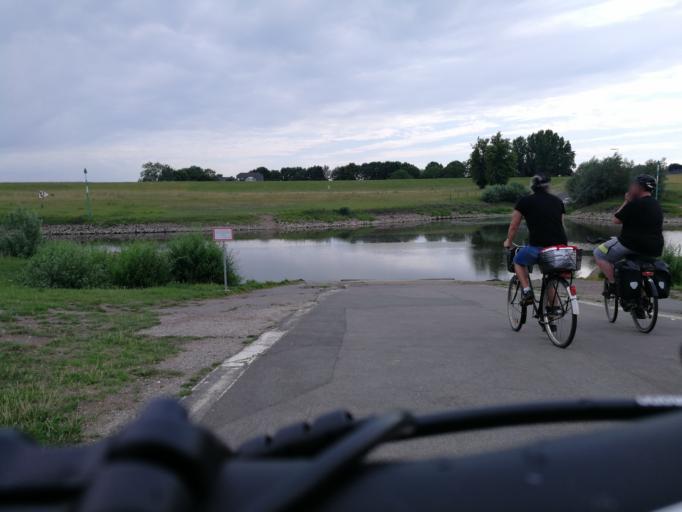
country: DE
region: North Rhine-Westphalia
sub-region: Regierungsbezirk Dusseldorf
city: Kleve
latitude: 51.8320
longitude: 6.1104
